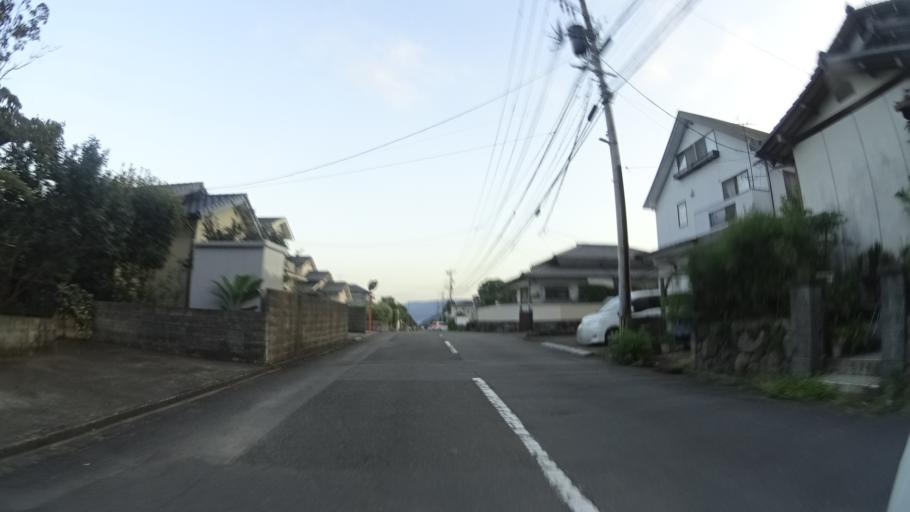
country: JP
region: Oita
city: Beppu
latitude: 33.3187
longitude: 131.4843
